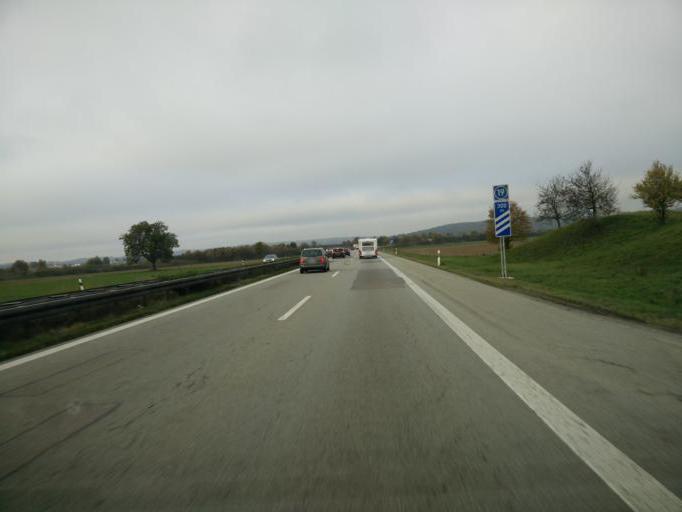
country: DE
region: Bavaria
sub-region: Swabia
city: Apfeltrach
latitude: 48.0309
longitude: 10.5193
